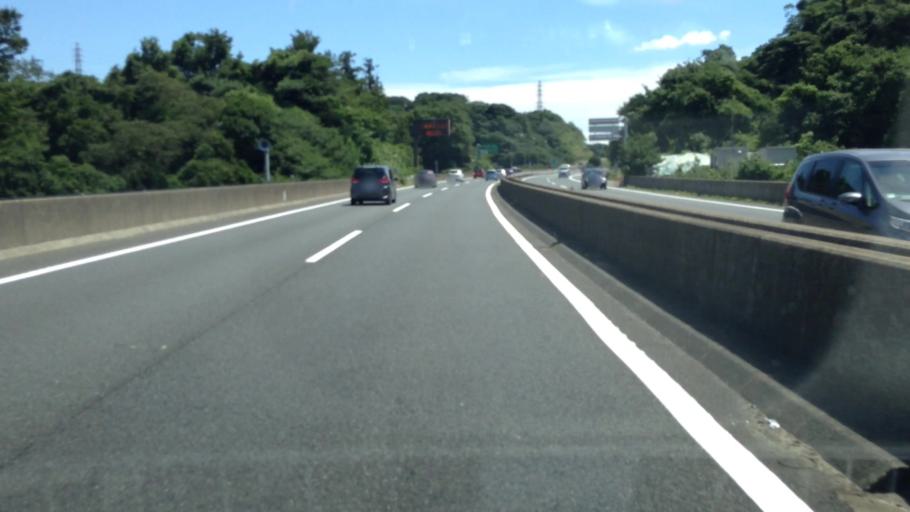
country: JP
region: Kanagawa
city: Yokosuka
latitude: 35.2812
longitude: 139.6296
